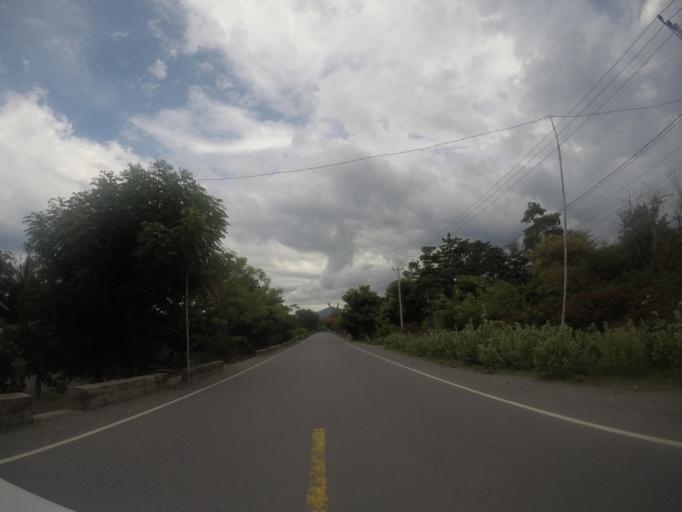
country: TL
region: Liquica
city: Liquica
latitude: -8.6046
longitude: 125.2880
